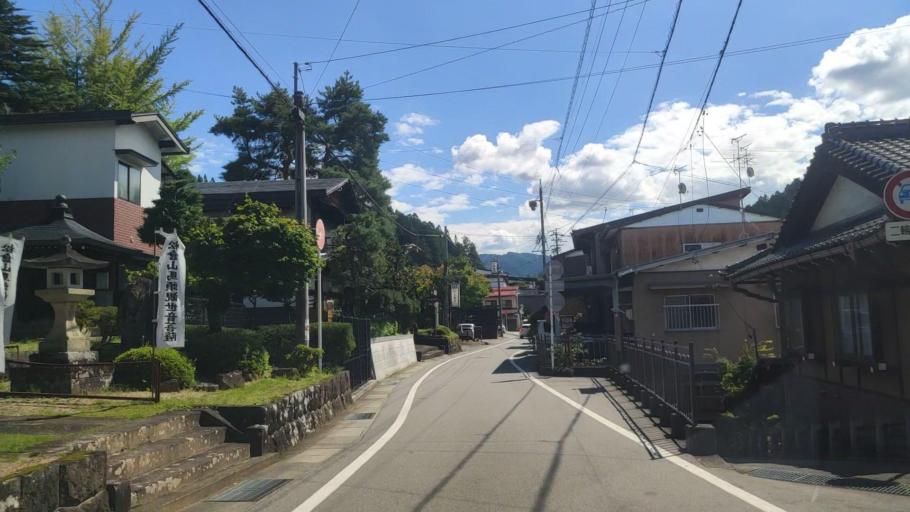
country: JP
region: Gifu
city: Takayama
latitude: 36.1436
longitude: 137.2648
